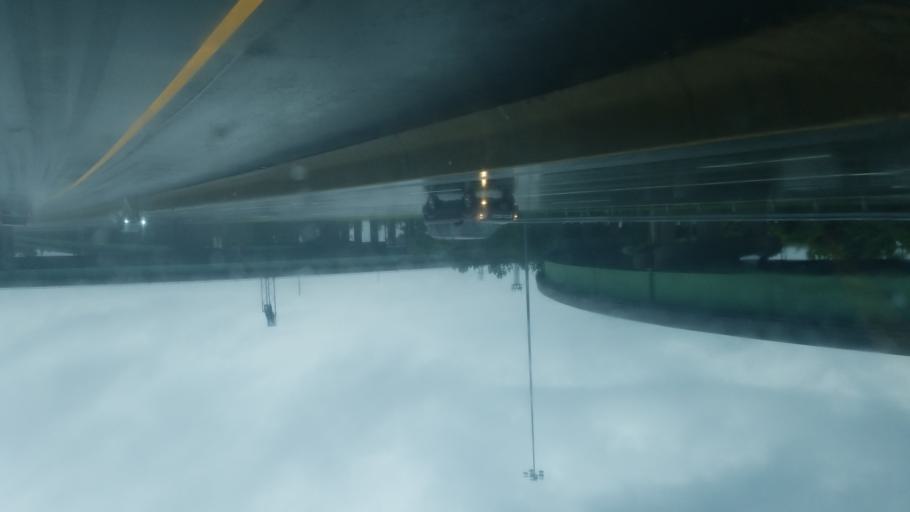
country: US
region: Virginia
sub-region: City of Newport News
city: Newport News
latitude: 36.9849
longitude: -76.4271
